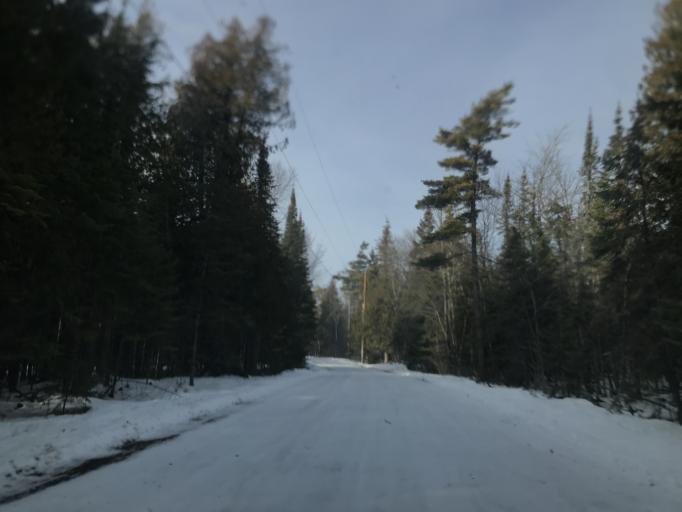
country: US
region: Wisconsin
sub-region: Door County
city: Sturgeon Bay
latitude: 45.1419
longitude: -87.0512
